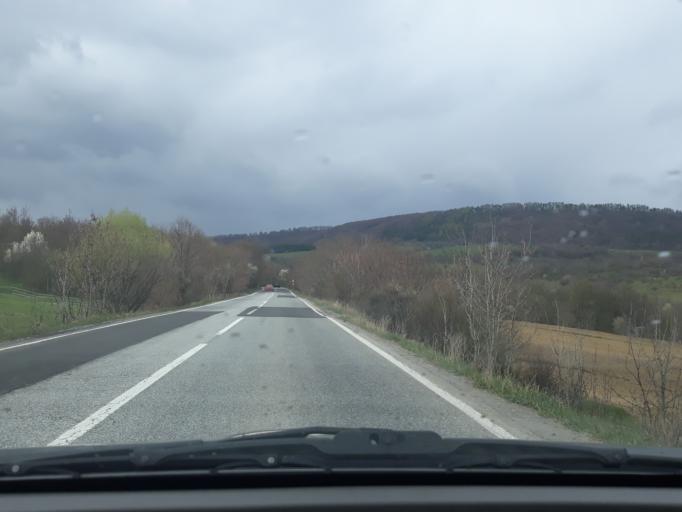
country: RO
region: Harghita
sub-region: Comuna Lupeni
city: Lupeni
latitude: 46.4012
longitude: 25.2160
